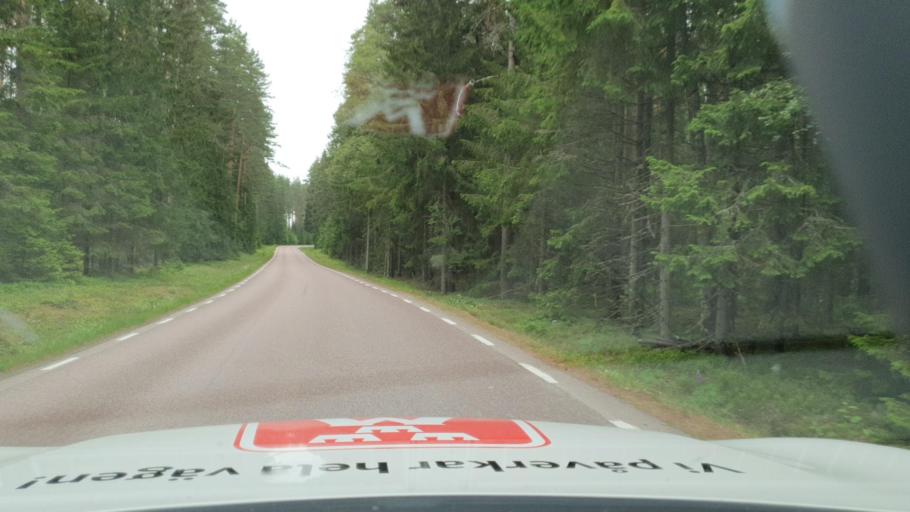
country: SE
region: Vaermland
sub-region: Kristinehamns Kommun
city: Kristinehamn
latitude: 59.4546
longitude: 13.9428
